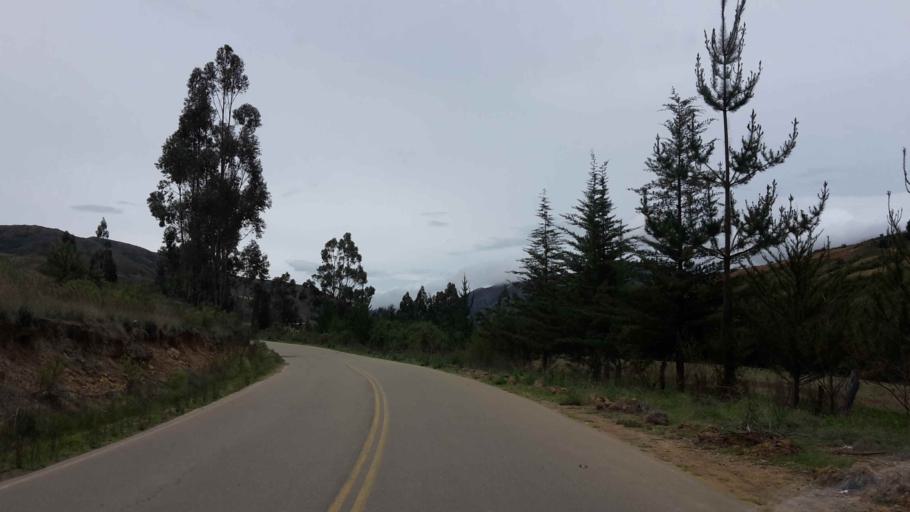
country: BO
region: Cochabamba
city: Totora
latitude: -17.6710
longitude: -65.2201
